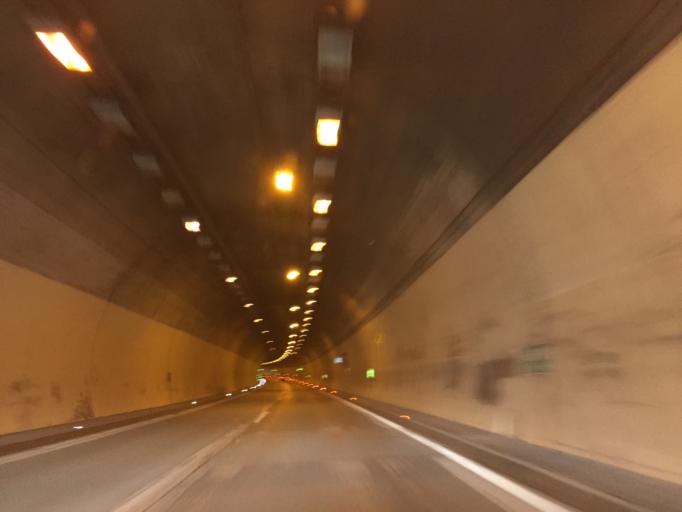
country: AT
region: Salzburg
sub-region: Politischer Bezirk Sankt Johann im Pongau
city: Werfen
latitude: 47.4923
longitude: 13.1823
